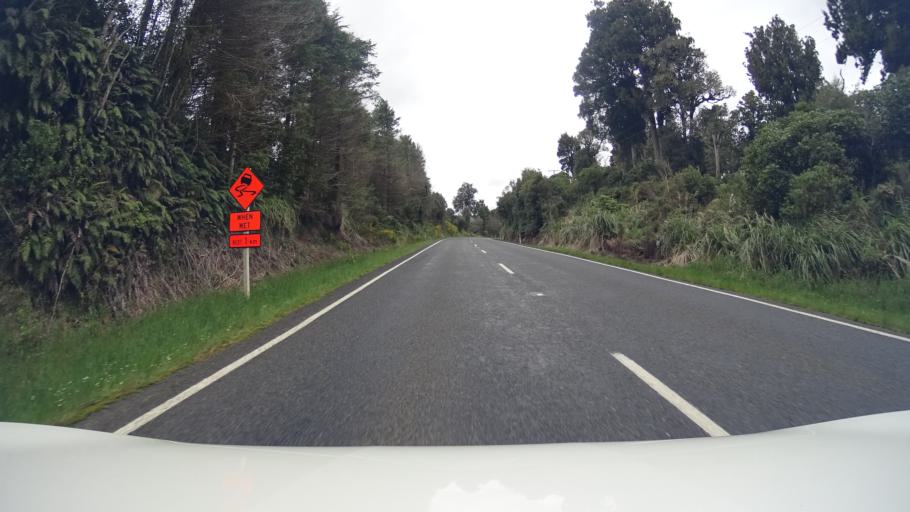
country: NZ
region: Manawatu-Wanganui
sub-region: Ruapehu District
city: Waiouru
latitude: -39.2376
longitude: 175.3916
